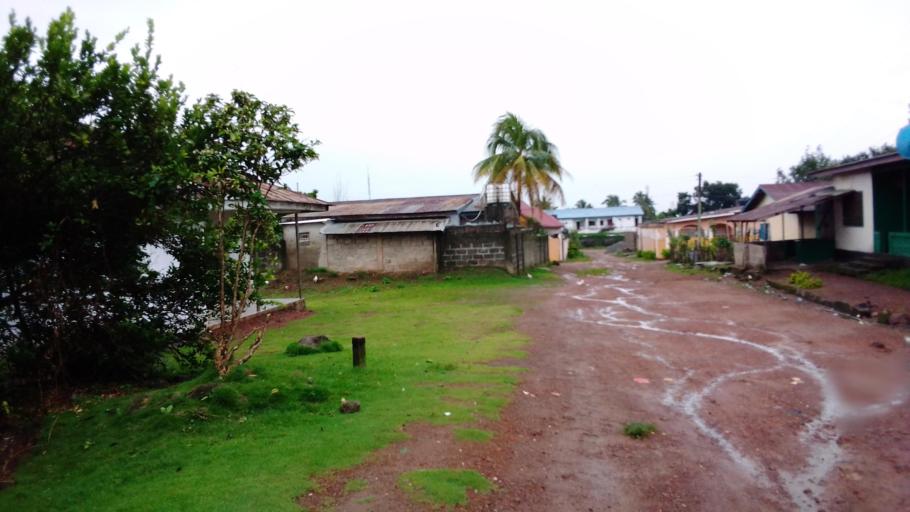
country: SL
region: Eastern Province
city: Kenema
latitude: 7.8902
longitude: -11.1892
